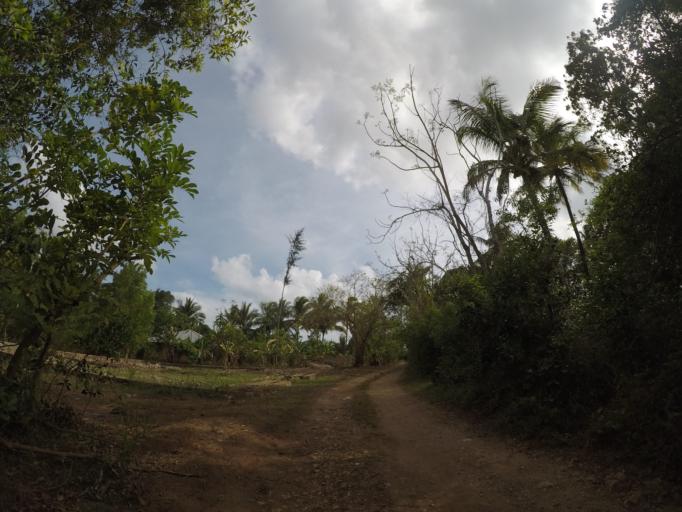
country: TZ
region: Zanzibar Central/South
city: Koani
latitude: -6.2196
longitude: 39.3205
